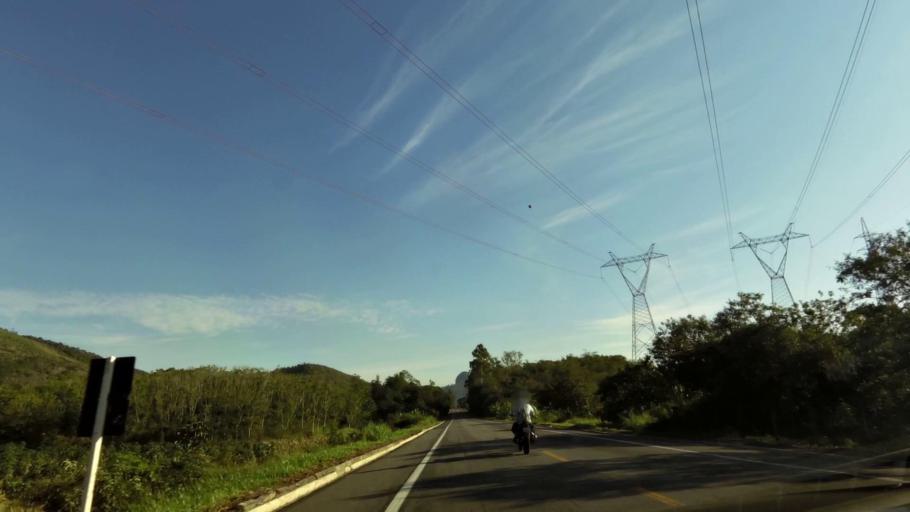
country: BR
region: Espirito Santo
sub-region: Guarapari
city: Guarapari
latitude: -20.5551
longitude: -40.4806
